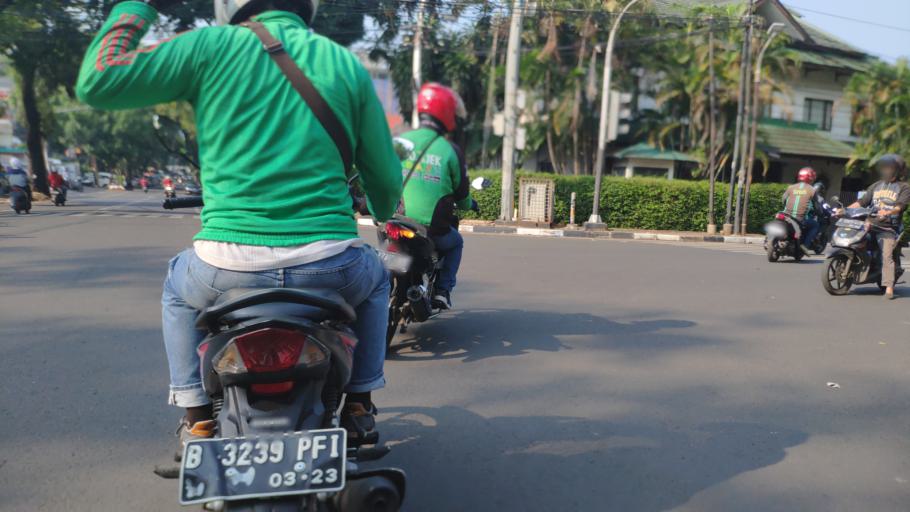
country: ID
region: Jakarta Raya
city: Jakarta
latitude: -6.2467
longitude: 106.7920
